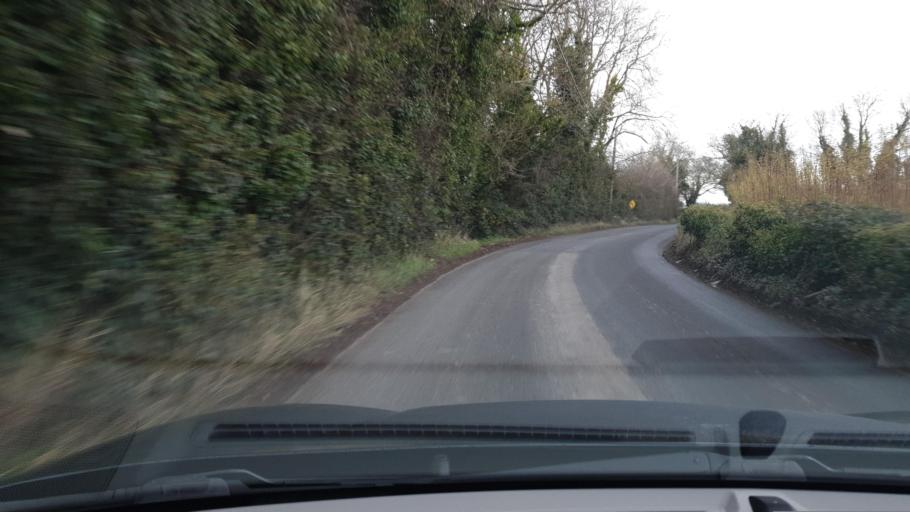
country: IE
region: Leinster
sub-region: An Mhi
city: Ashbourne
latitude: 53.5330
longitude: -6.4067
